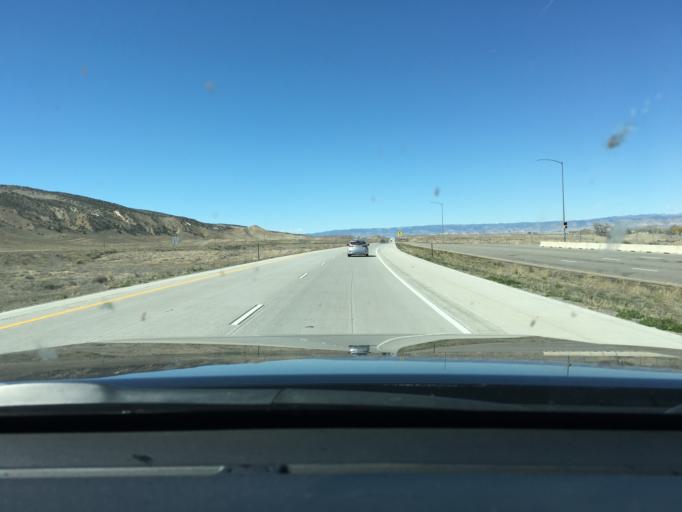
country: US
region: Colorado
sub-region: Mesa County
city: Loma
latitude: 39.1806
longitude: -108.8254
